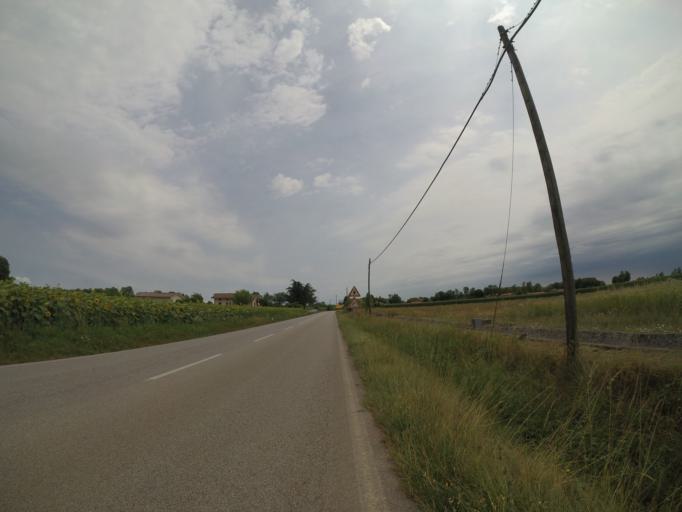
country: IT
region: Friuli Venezia Giulia
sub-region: Provincia di Udine
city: Sedegliano
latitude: 46.0043
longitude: 12.9901
